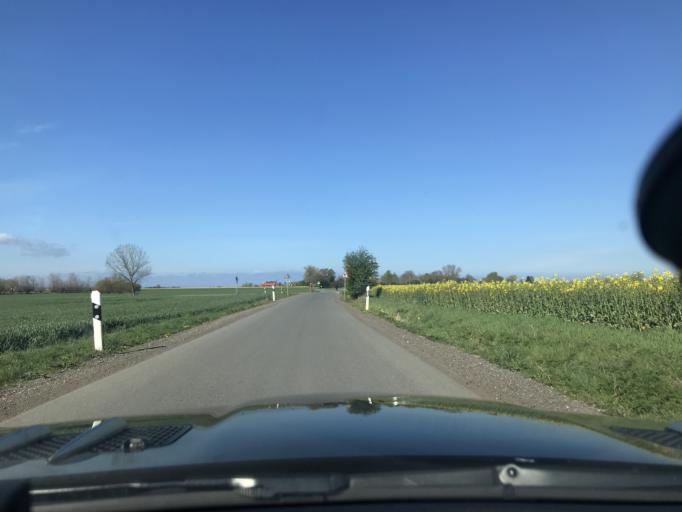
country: DE
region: Schleswig-Holstein
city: Grossenbrode
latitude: 54.4260
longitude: 11.1204
